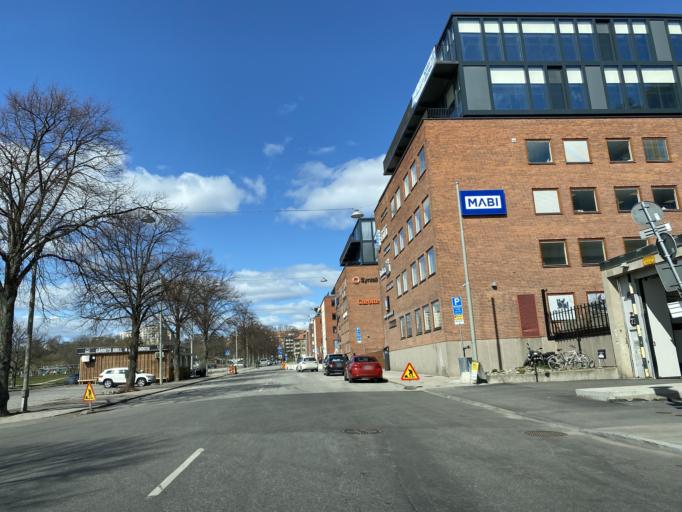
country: SE
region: Stockholm
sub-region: Stockholms Kommun
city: OEstermalm
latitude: 59.3403
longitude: 18.1115
